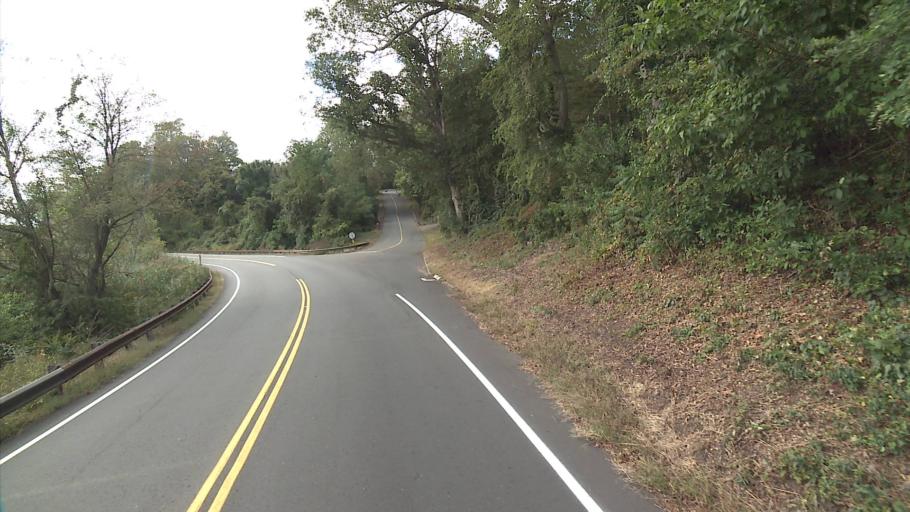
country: US
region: Connecticut
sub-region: Middlesex County
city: Chester Center
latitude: 41.4104
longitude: -72.4435
